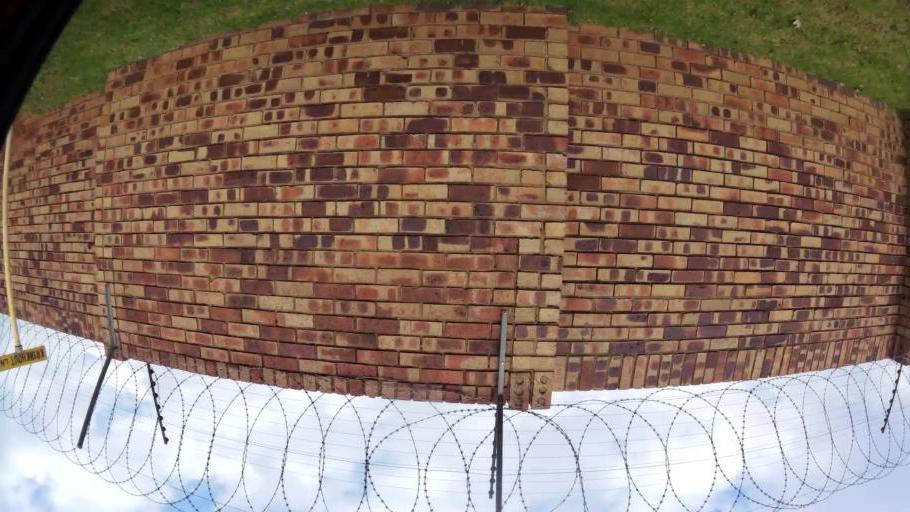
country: ZA
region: Gauteng
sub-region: Sedibeng District Municipality
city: Vanderbijlpark
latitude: -26.7066
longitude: 27.8247
